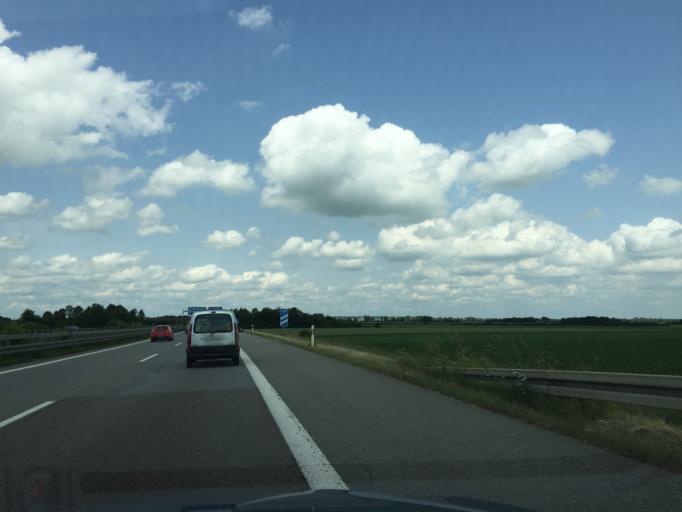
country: DE
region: Bavaria
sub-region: Swabia
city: Nersingen
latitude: 48.4527
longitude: 10.1170
